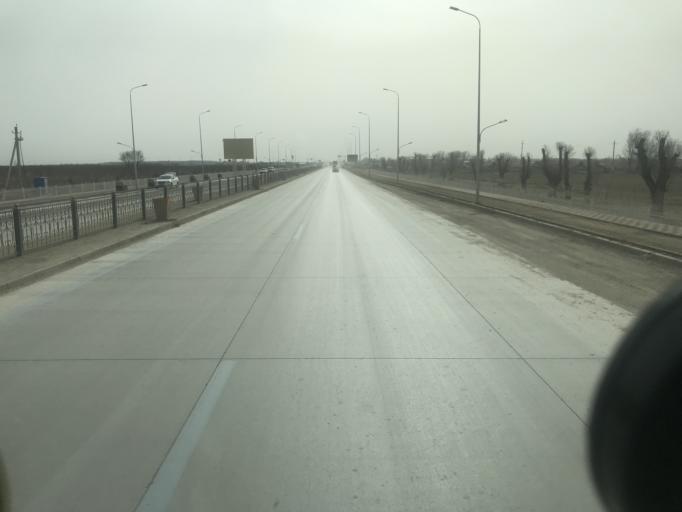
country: KZ
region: Ongtustik Qazaqstan
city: Turkestan
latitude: 43.2692
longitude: 68.3527
